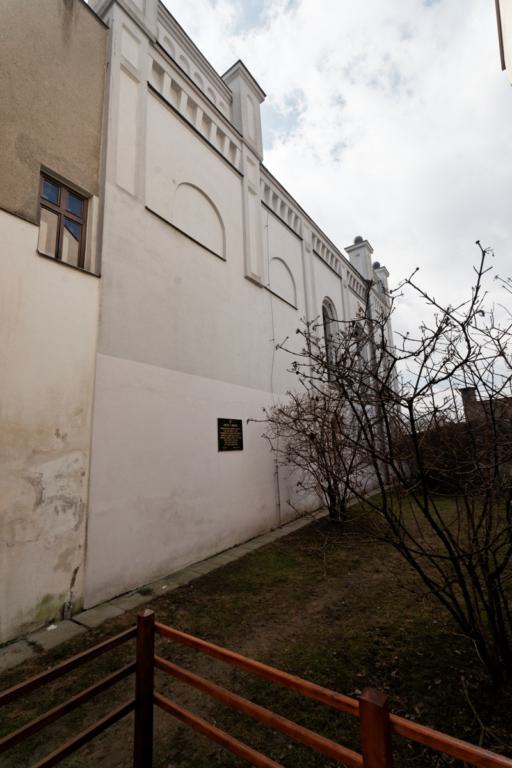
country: CZ
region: Olomoucky
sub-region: Okres Prerov
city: Hranice
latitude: 49.5489
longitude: 17.7341
